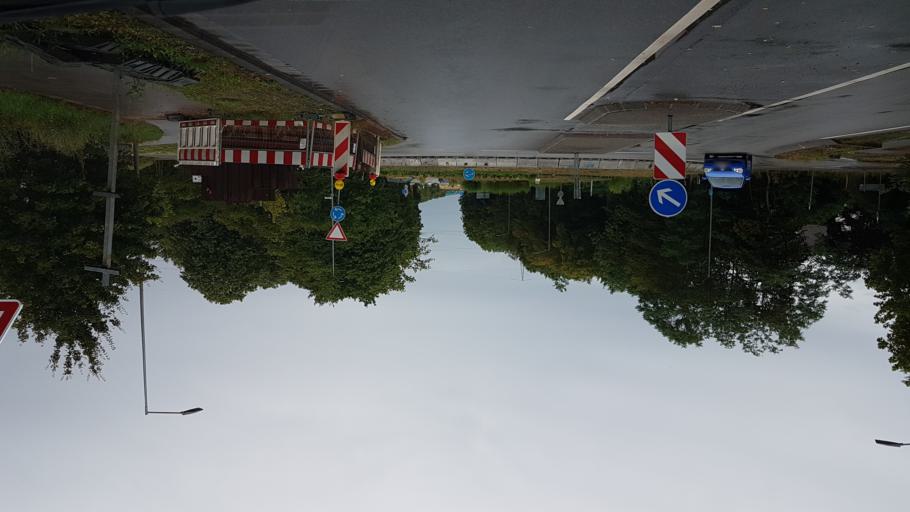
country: DE
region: Saarland
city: Saarwellingen
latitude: 49.3361
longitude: 6.7839
